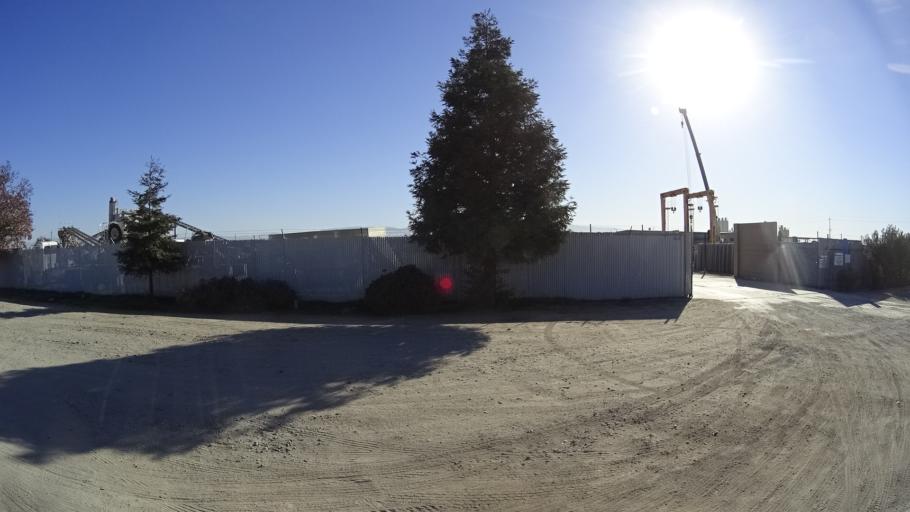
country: US
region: California
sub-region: Kern County
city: Greenfield
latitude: 35.2816
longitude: -119.0944
